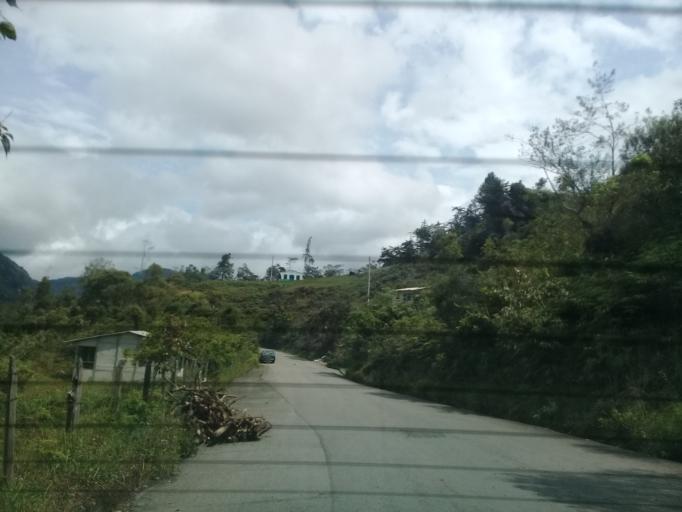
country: CO
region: Cundinamarca
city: Gachala
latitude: 4.6993
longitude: -73.4793
